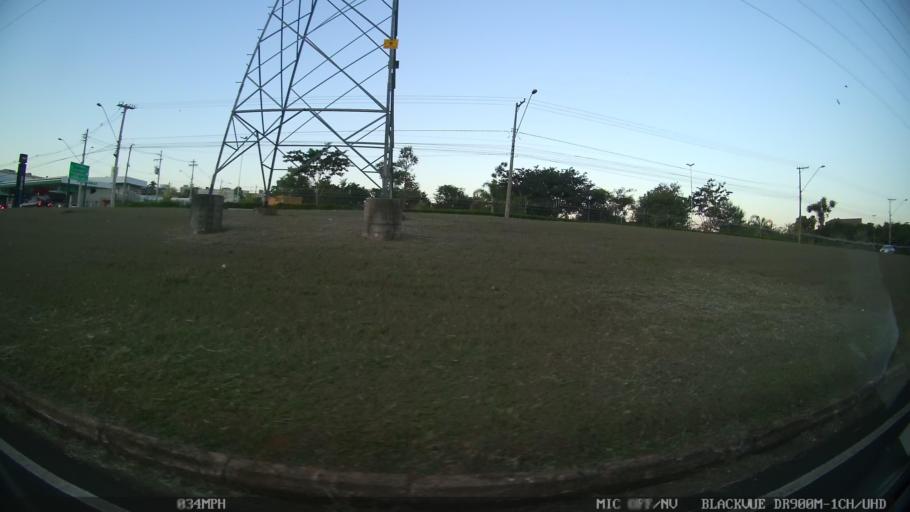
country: BR
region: Sao Paulo
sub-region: Sao Jose Do Rio Preto
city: Sao Jose do Rio Preto
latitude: -20.8120
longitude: -49.3406
